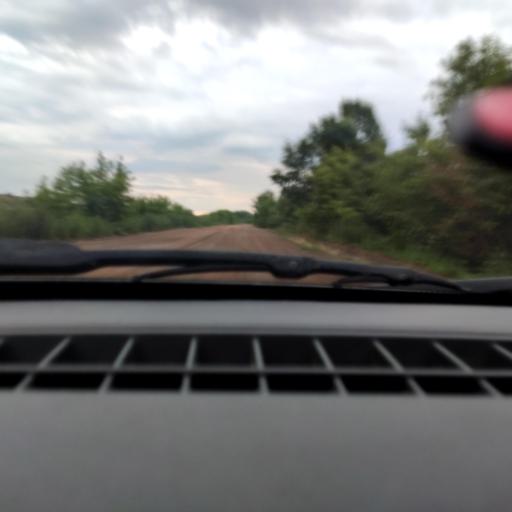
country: RU
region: Bashkortostan
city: Blagoveshchensk
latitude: 54.9251
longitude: 55.9713
